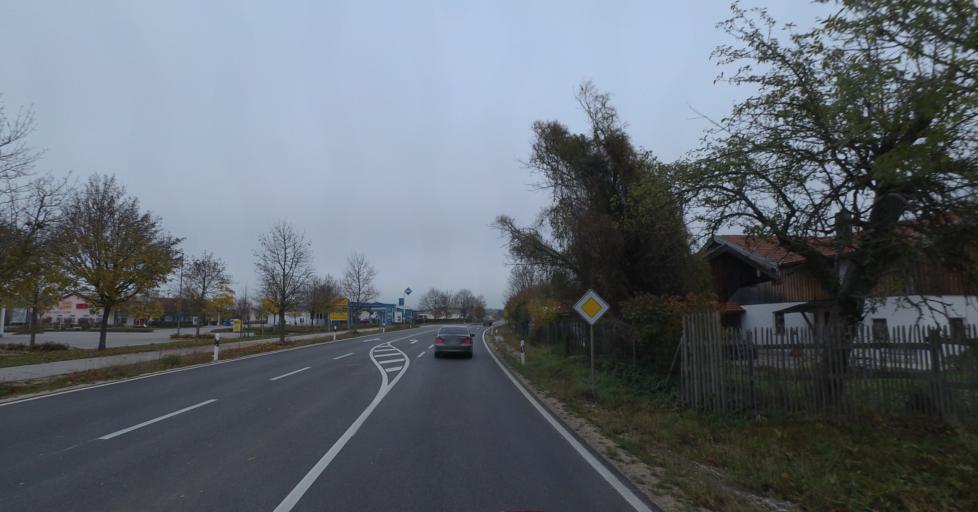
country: DE
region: Bavaria
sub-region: Upper Bavaria
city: Garching an der Alz
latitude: 48.1250
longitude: 12.5749
